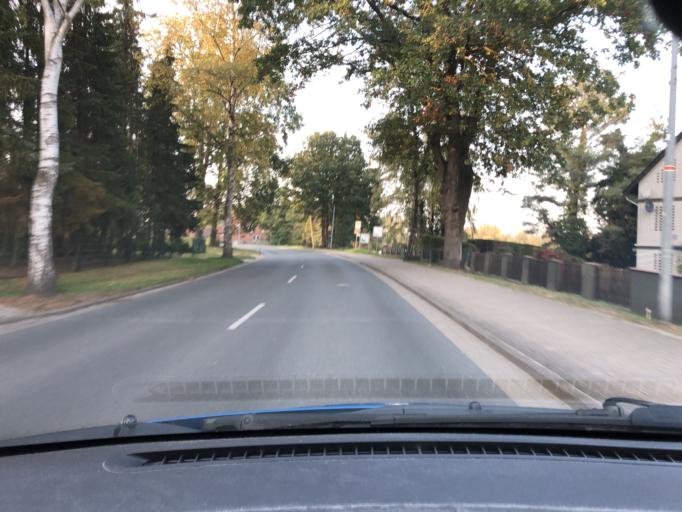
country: DE
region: Lower Saxony
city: Hitzacker
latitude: 53.1374
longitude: 11.0459
